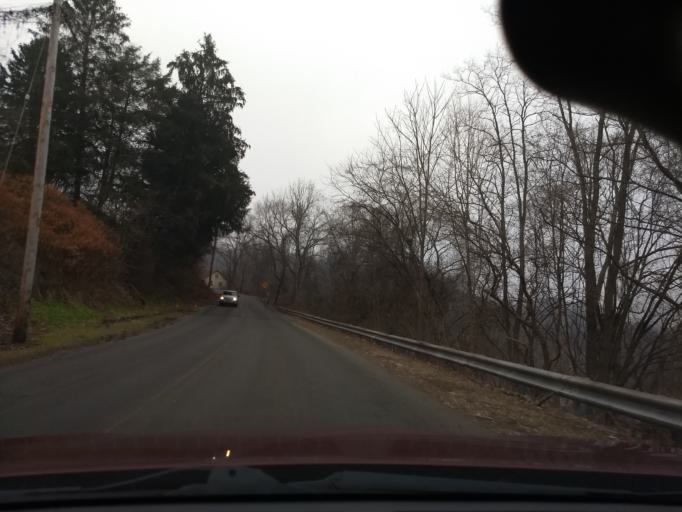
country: US
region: Pennsylvania
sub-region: Allegheny County
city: East Pittsburgh
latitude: 40.3853
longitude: -79.8296
